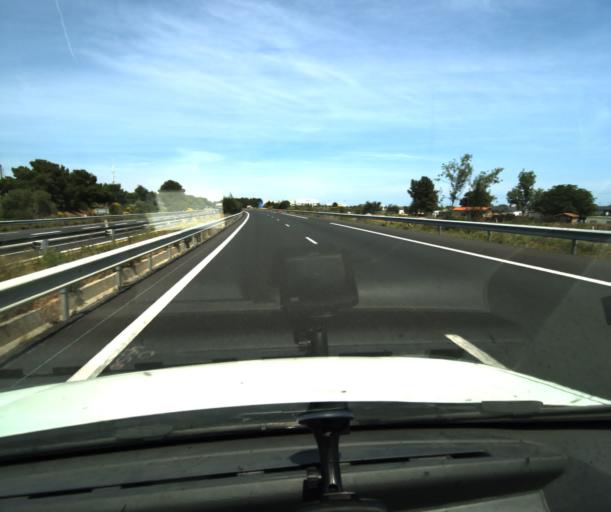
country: FR
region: Languedoc-Roussillon
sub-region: Departement des Pyrenees-Orientales
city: Pia
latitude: 42.7455
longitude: 2.8913
